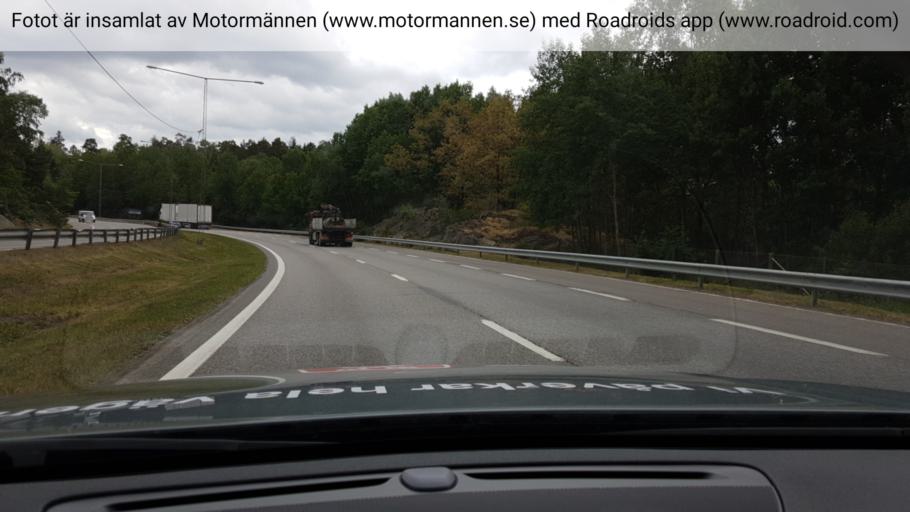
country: SE
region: Stockholm
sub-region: Huddinge Kommun
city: Huddinge
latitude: 59.2678
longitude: 18.0059
